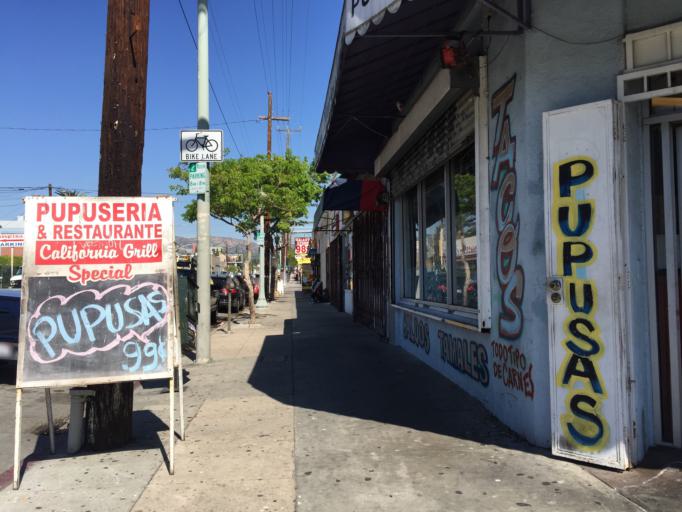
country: US
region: California
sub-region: Los Angeles County
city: Silver Lake
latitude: 34.0857
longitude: -118.2868
